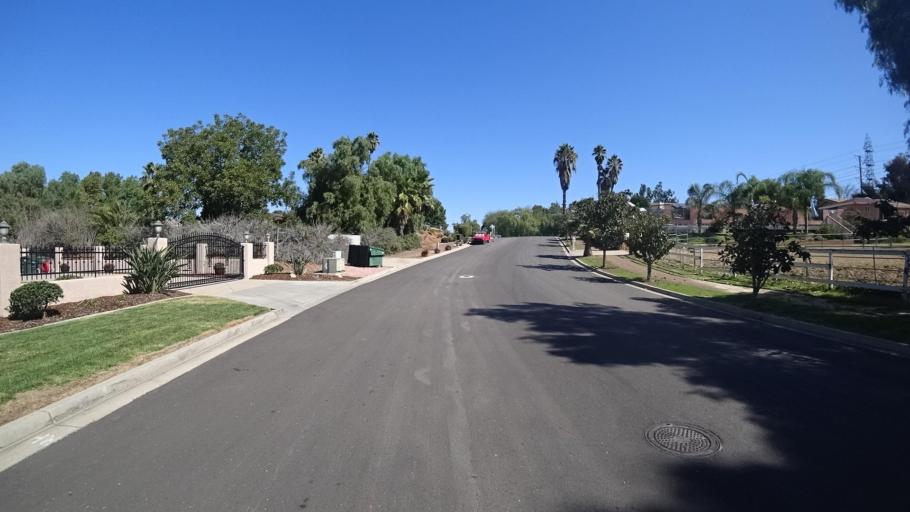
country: US
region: California
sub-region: San Diego County
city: Rancho San Diego
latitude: 32.7399
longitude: -116.9154
